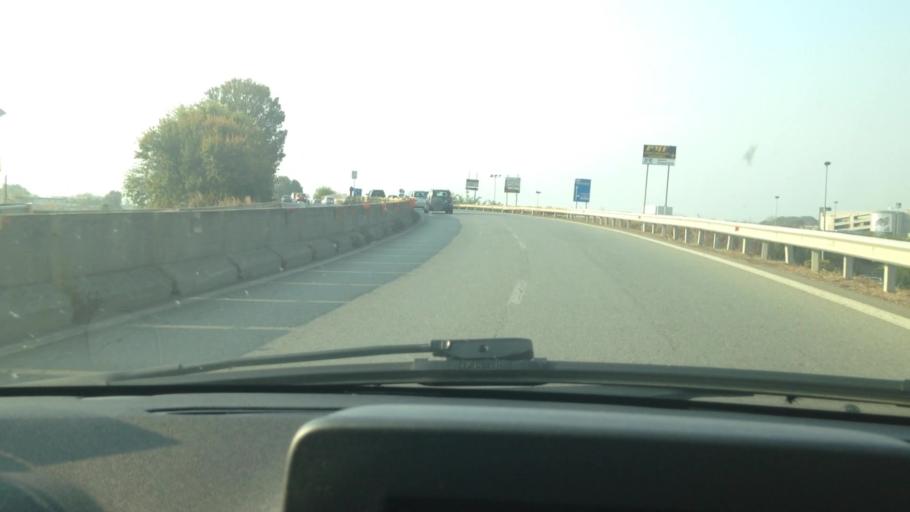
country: IT
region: Piedmont
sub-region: Provincia di Torino
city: Caselle Torinese
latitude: 45.1864
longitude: 7.6444
